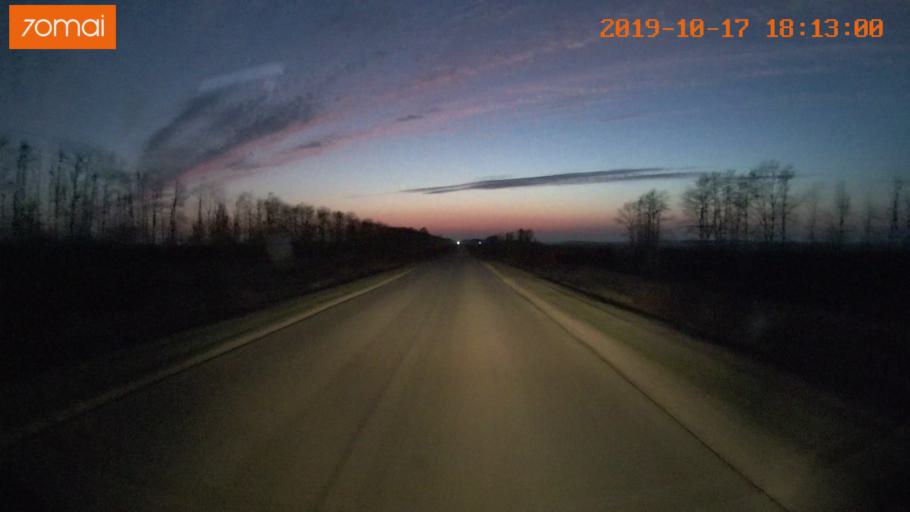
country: RU
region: Tula
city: Kurkino
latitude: 53.4111
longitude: 38.5986
